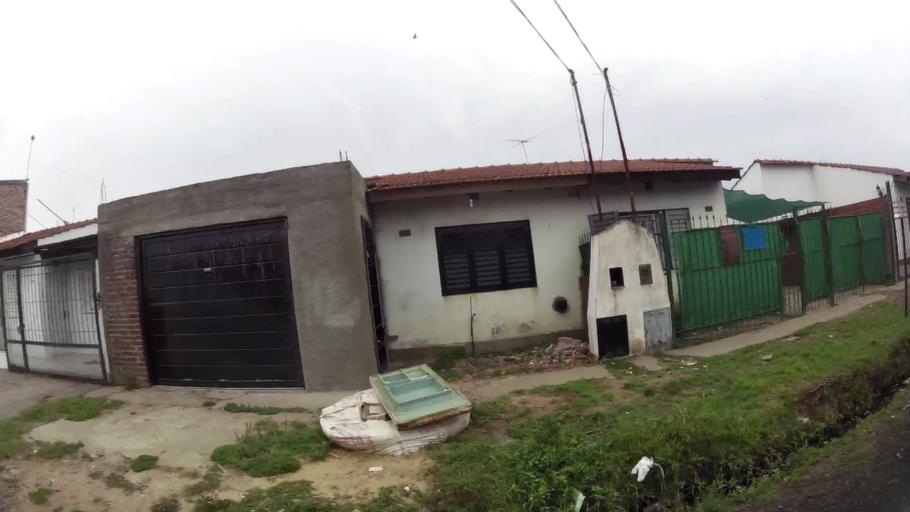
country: AR
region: Buenos Aires
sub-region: Partido de Campana
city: Campana
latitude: -34.1858
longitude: -58.9368
